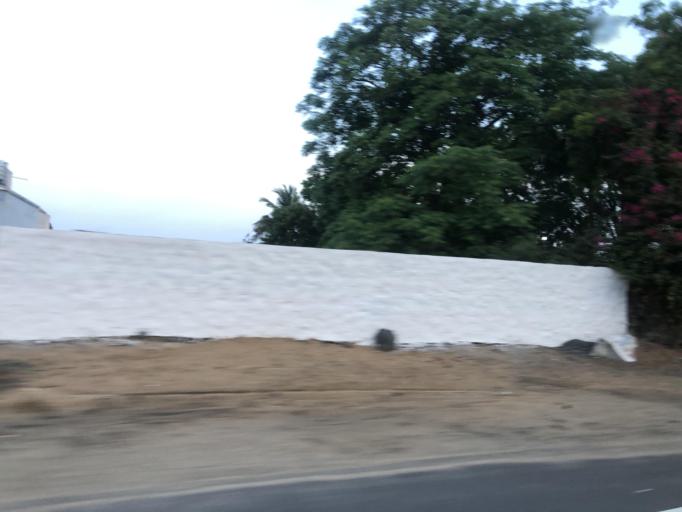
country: IN
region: Tamil Nadu
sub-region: Kancheepuram
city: Mamallapuram
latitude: 12.7480
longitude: 80.2401
